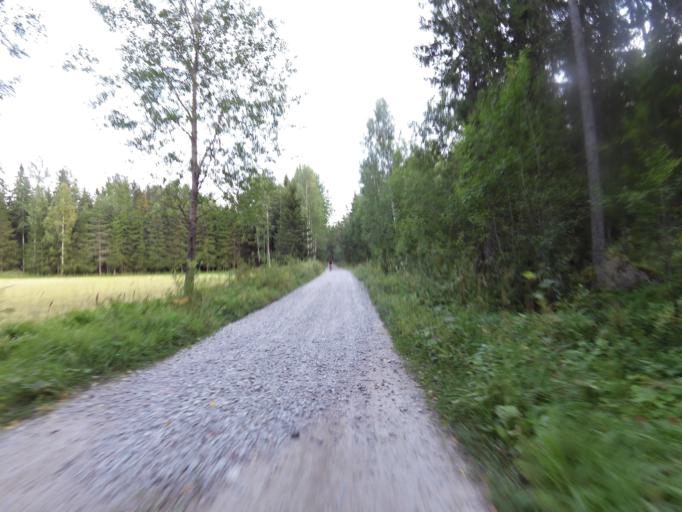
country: SE
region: Gaevleborg
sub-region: Gavle Kommun
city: Gavle
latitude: 60.7076
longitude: 17.1223
